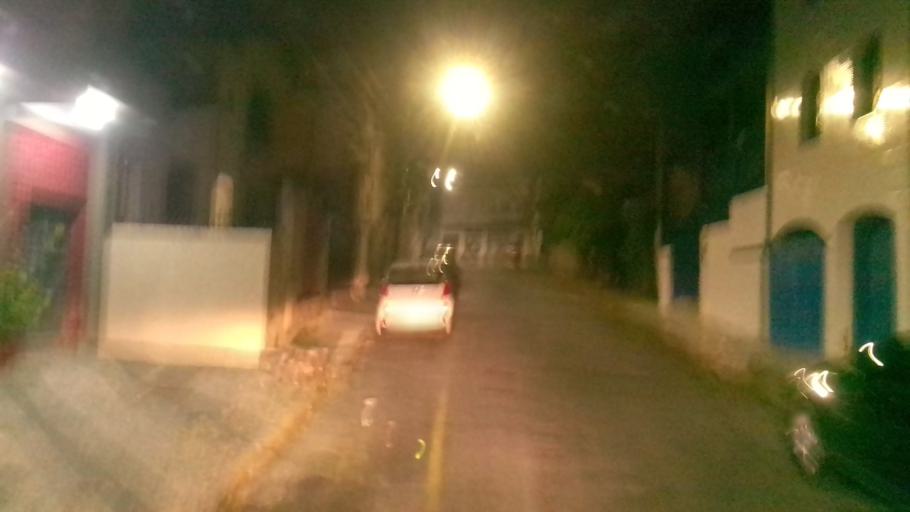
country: BR
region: Minas Gerais
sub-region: Belo Horizonte
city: Belo Horizonte
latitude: -19.9106
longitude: -43.9618
